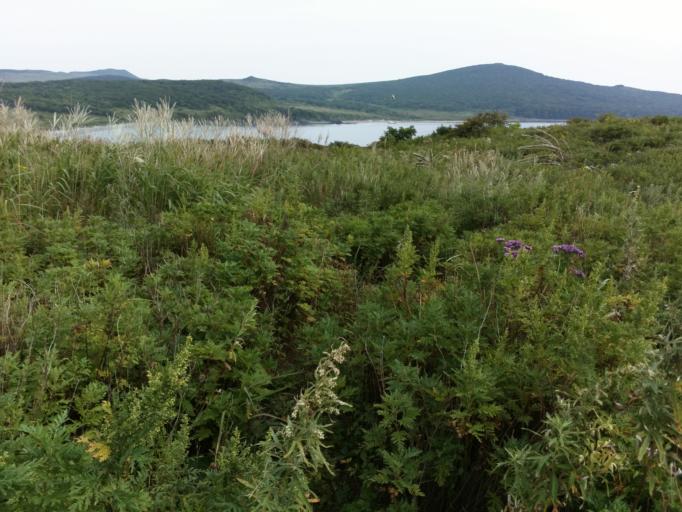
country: RU
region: Primorskiy
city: Popova
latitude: 42.9200
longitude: 131.7120
